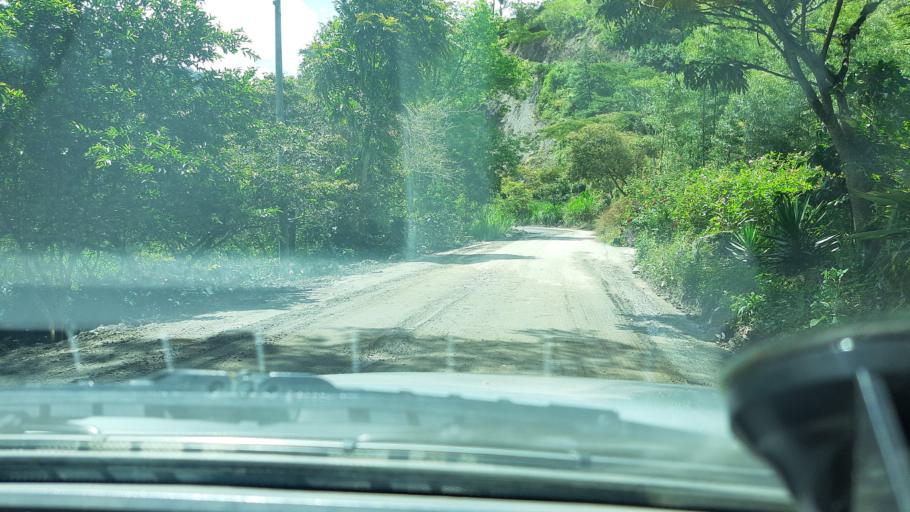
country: CO
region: Boyaca
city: Chinavita
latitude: 5.1802
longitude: -73.3827
